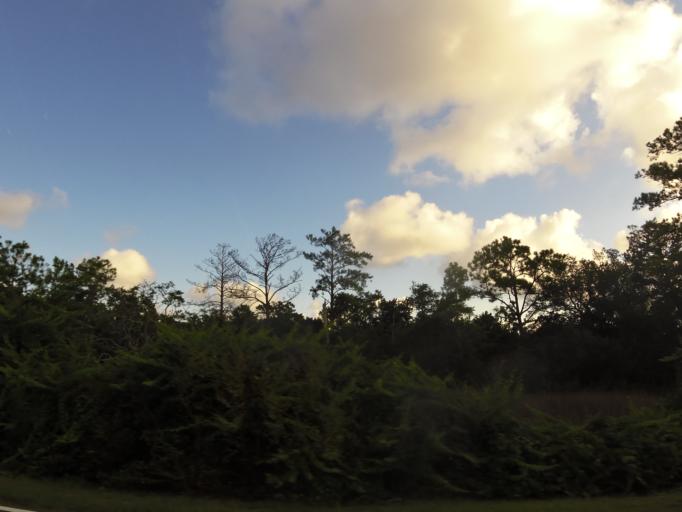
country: US
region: Georgia
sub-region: Glynn County
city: Saint Simon Mills
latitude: 31.1849
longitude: -81.3843
